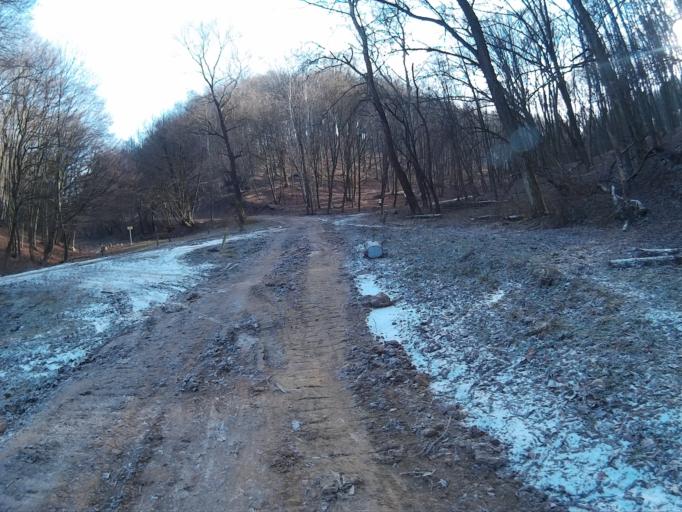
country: HU
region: Fejer
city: Szarliget
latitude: 47.5005
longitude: 18.4126
